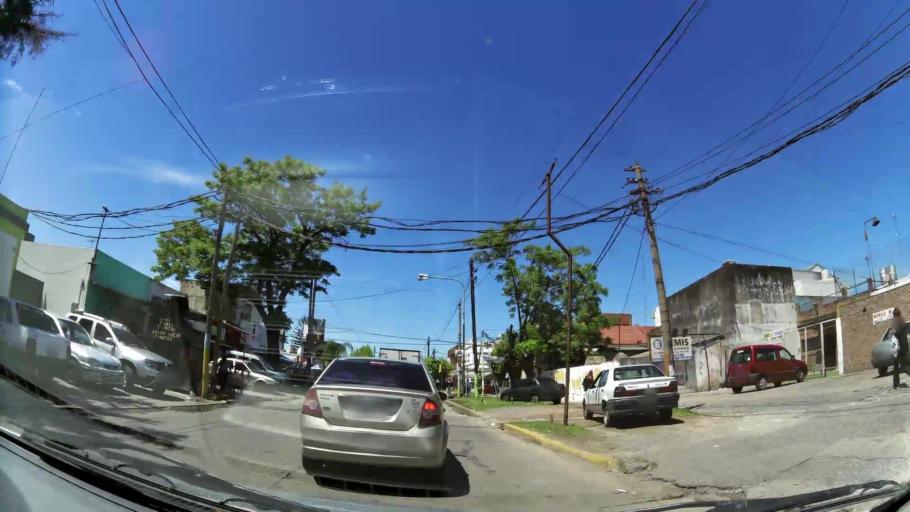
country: AR
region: Buenos Aires
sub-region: Partido de Quilmes
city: Quilmes
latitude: -34.7320
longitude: -58.2700
